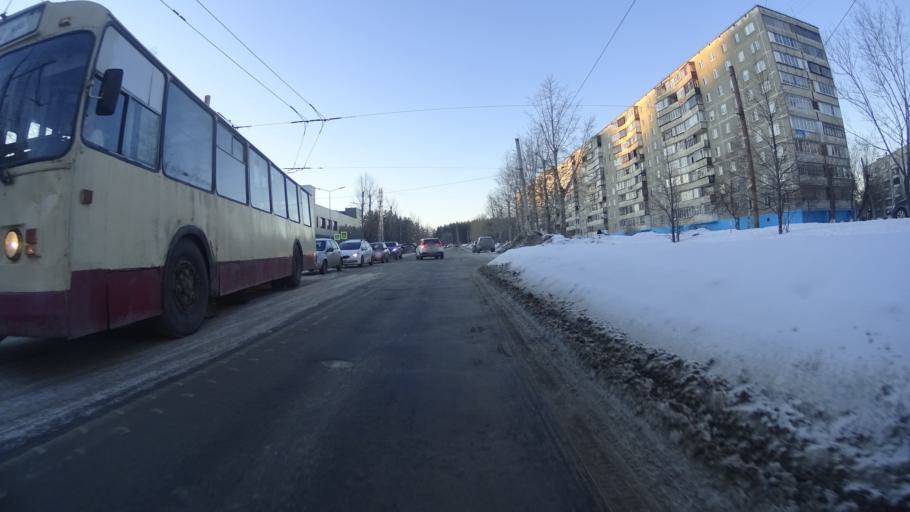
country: RU
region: Chelyabinsk
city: Roshchino
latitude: 55.1946
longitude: 61.3002
